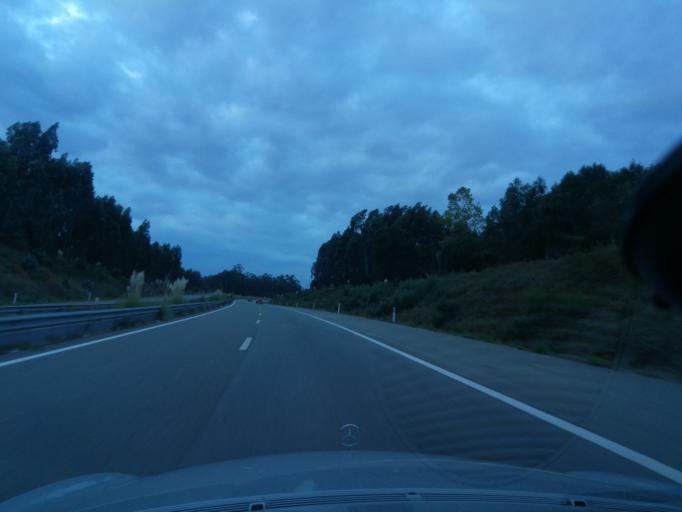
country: PT
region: Aveiro
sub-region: Estarreja
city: Beduido
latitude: 40.7696
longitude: -8.5560
